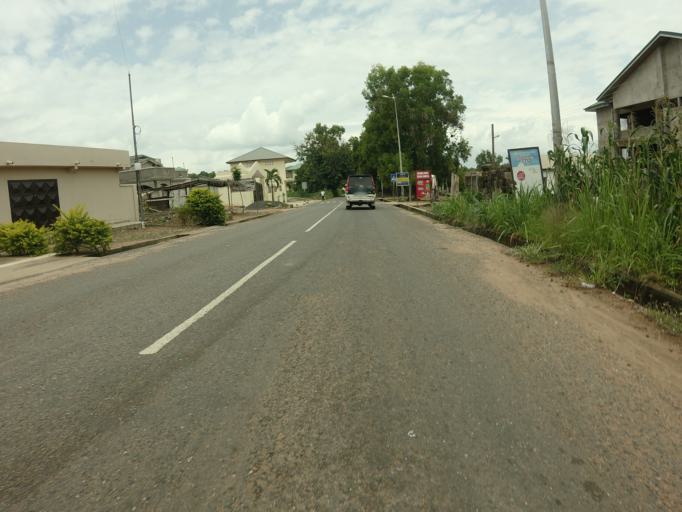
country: GH
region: Volta
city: Ho
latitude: 6.5999
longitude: 0.4624
